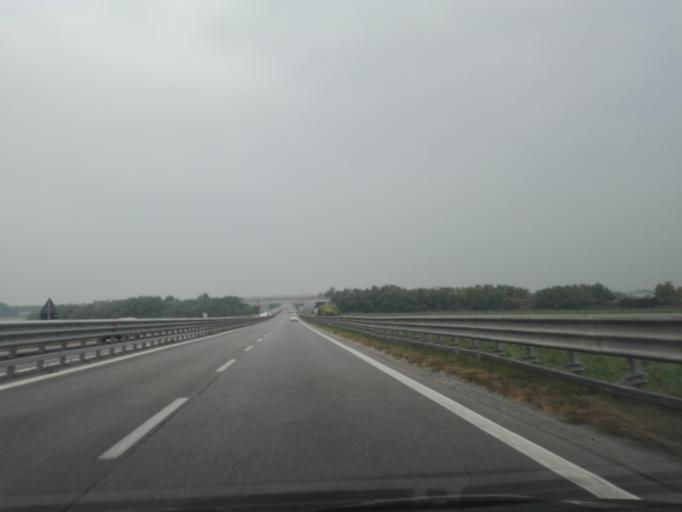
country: IT
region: Veneto
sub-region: Provincia di Verona
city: Legnago
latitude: 45.1672
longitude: 11.2986
